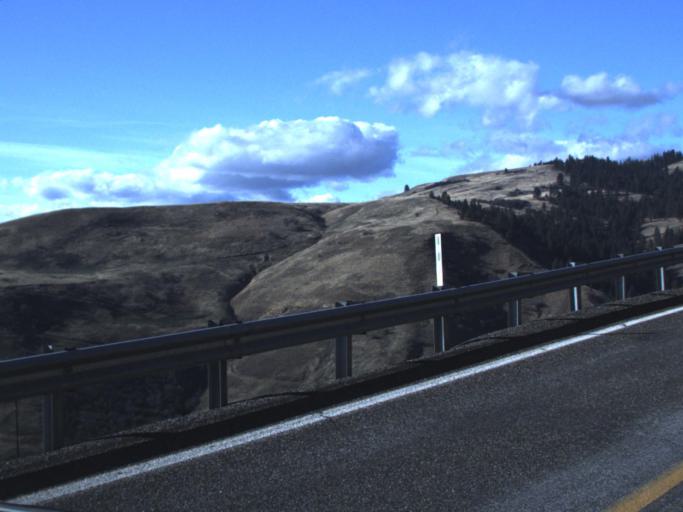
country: US
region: Washington
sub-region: Asotin County
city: Asotin
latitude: 46.0623
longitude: -117.2320
